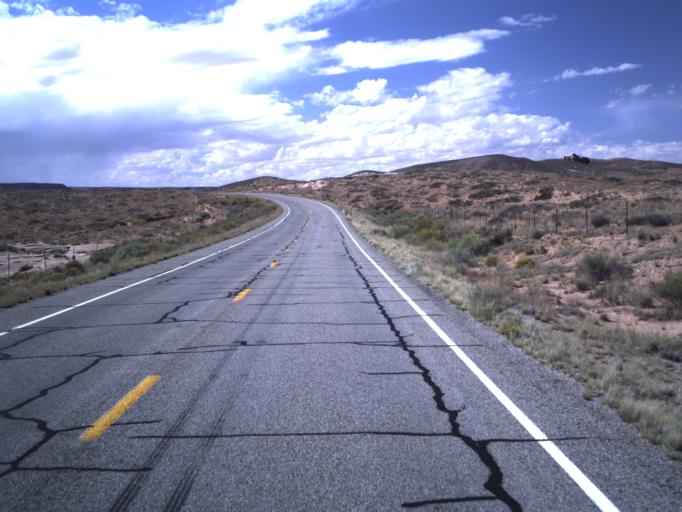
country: US
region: Utah
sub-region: San Juan County
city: Blanding
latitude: 37.2946
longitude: -109.4845
